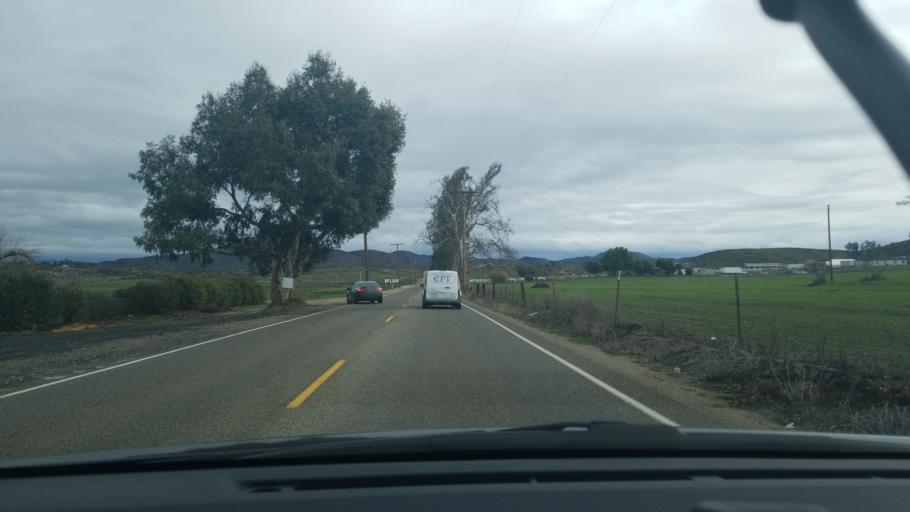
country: US
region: California
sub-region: Riverside County
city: Winchester
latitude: 33.6417
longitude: -117.1047
